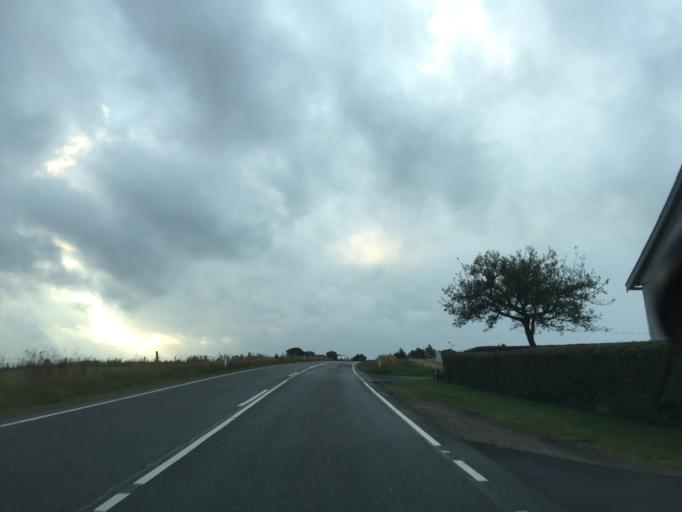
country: DK
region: Central Jutland
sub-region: Skanderborg Kommune
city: Ry
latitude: 56.1378
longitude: 9.8249
